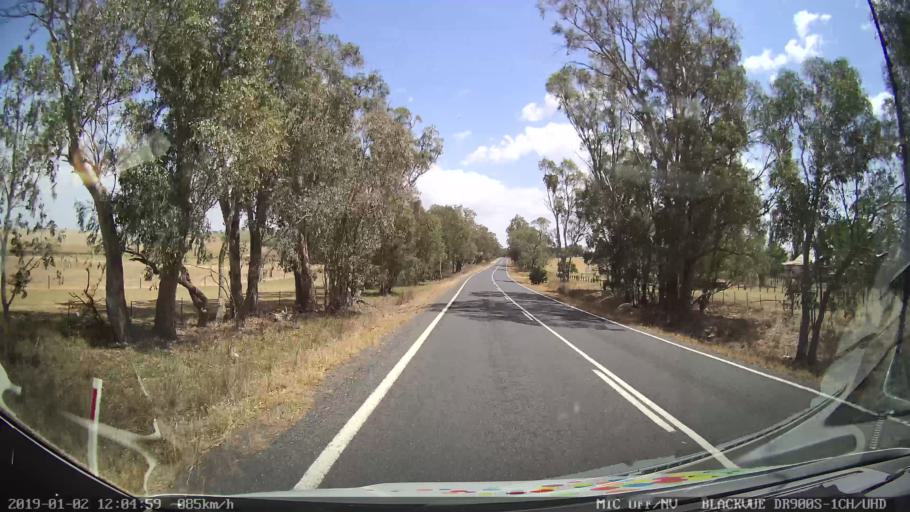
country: AU
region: New South Wales
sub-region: Young
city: Young
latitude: -34.5194
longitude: 148.3050
